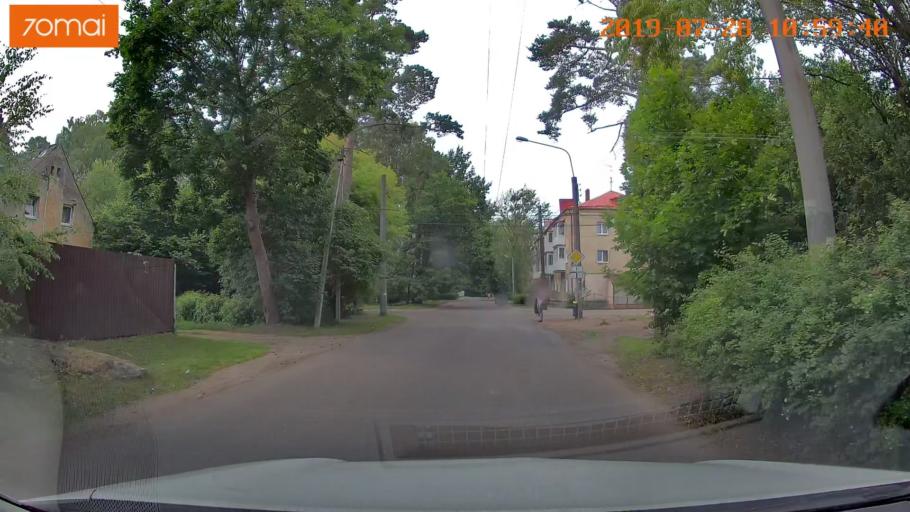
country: RU
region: Kaliningrad
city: Vzmorye
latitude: 54.7277
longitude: 20.3563
